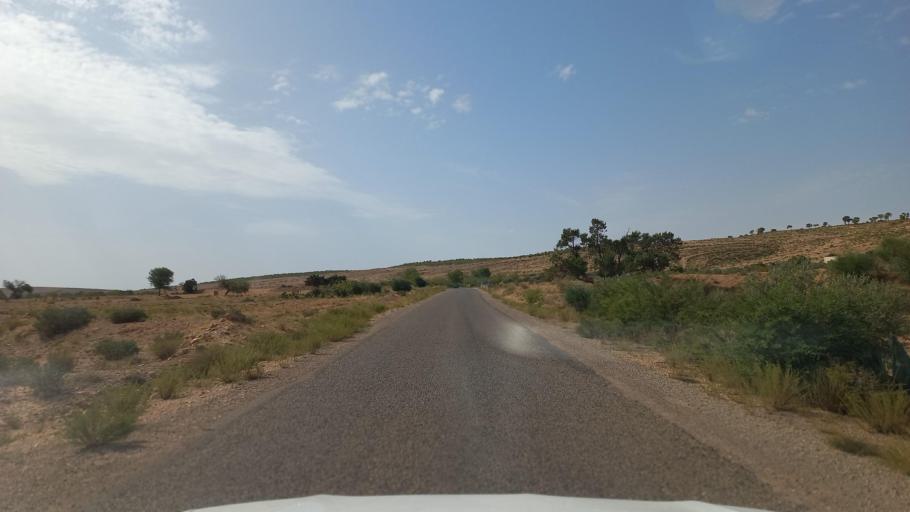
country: TN
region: Al Qasrayn
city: Kasserine
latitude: 35.3675
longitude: 8.8681
